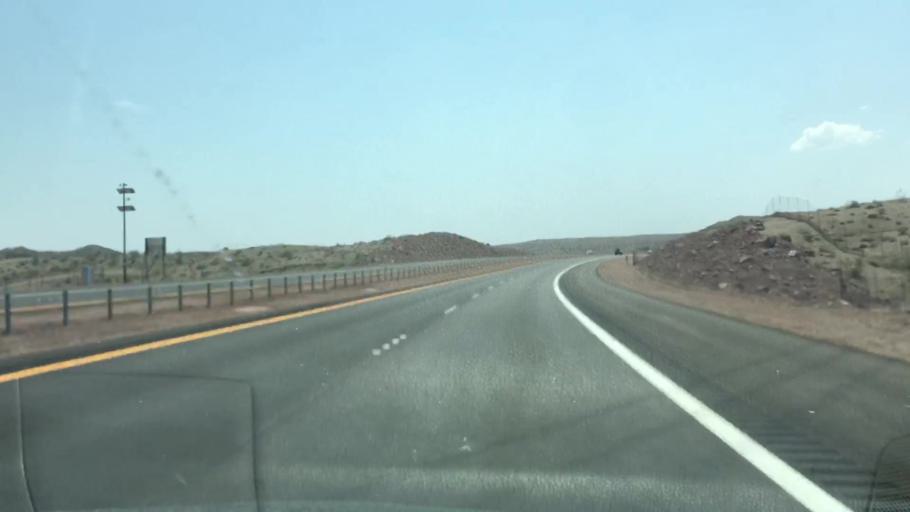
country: US
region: Nevada
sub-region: Clark County
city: Boulder City
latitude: 35.9791
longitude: -114.7925
